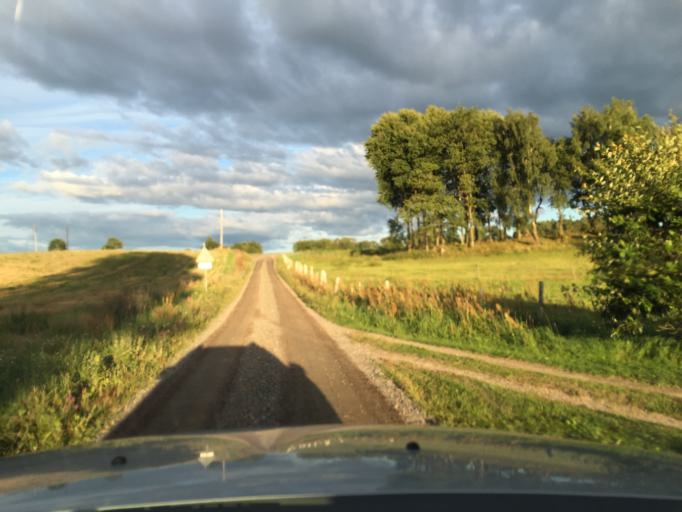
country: SE
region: Skane
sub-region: Hassleholms Kommun
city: Sosdala
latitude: 56.0267
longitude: 13.7483
